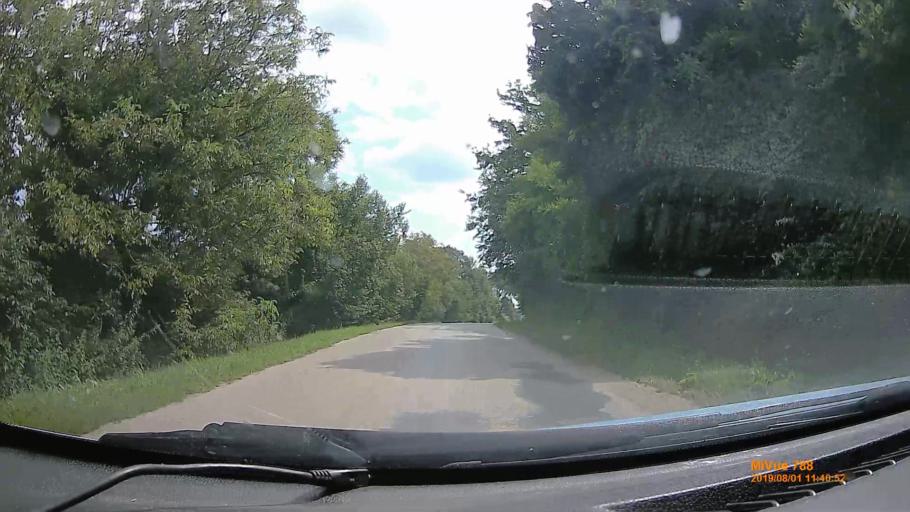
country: HU
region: Baranya
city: Villany
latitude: 45.8904
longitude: 18.3989
